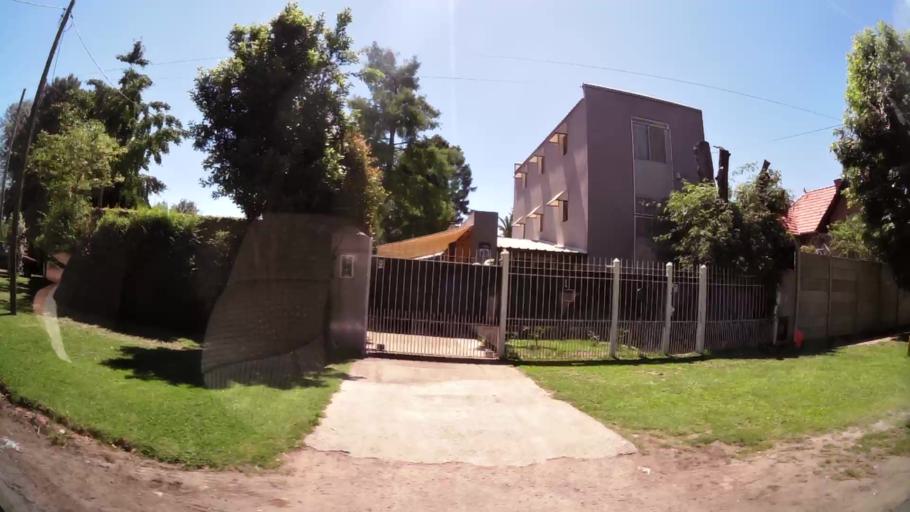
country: AR
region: Buenos Aires
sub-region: Partido de Tigre
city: Tigre
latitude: -34.4934
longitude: -58.6428
